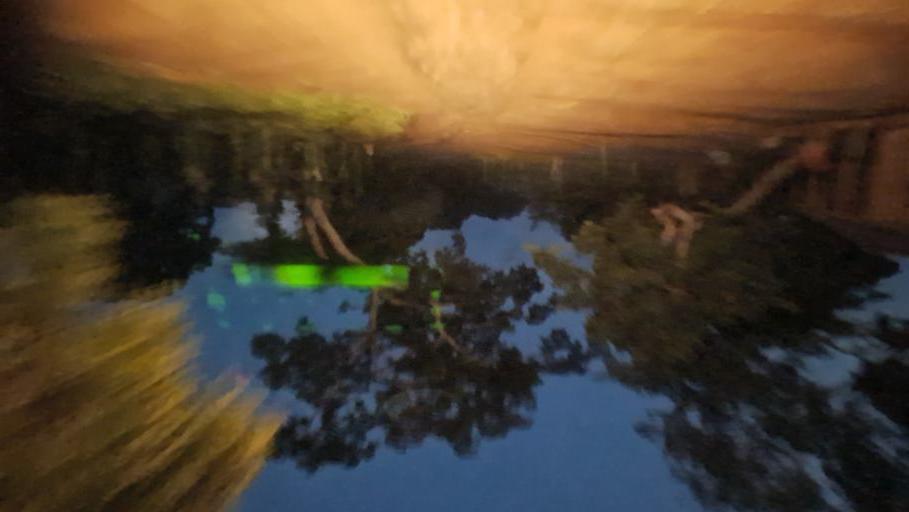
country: MZ
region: Nampula
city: Nampula
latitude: -14.6733
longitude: 39.8327
